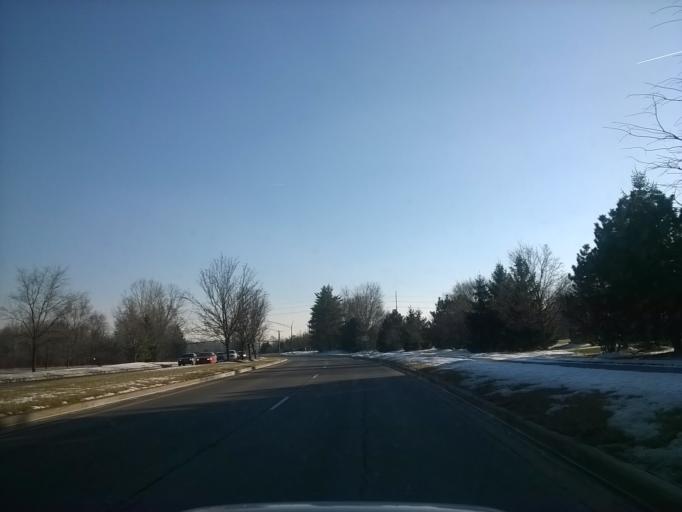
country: US
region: Indiana
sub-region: Hamilton County
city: Carmel
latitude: 39.9590
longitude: -86.0747
